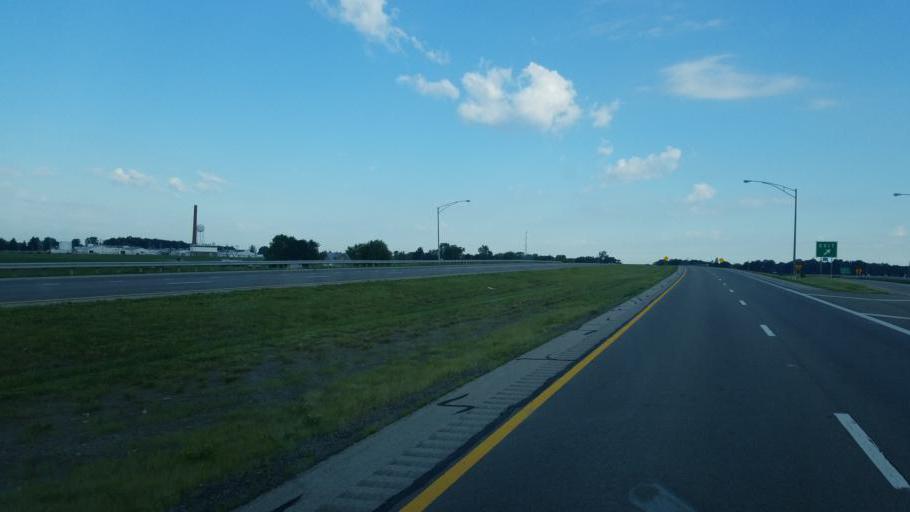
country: US
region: Ohio
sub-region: Crawford County
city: Bucyrus
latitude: 40.8090
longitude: -82.9290
